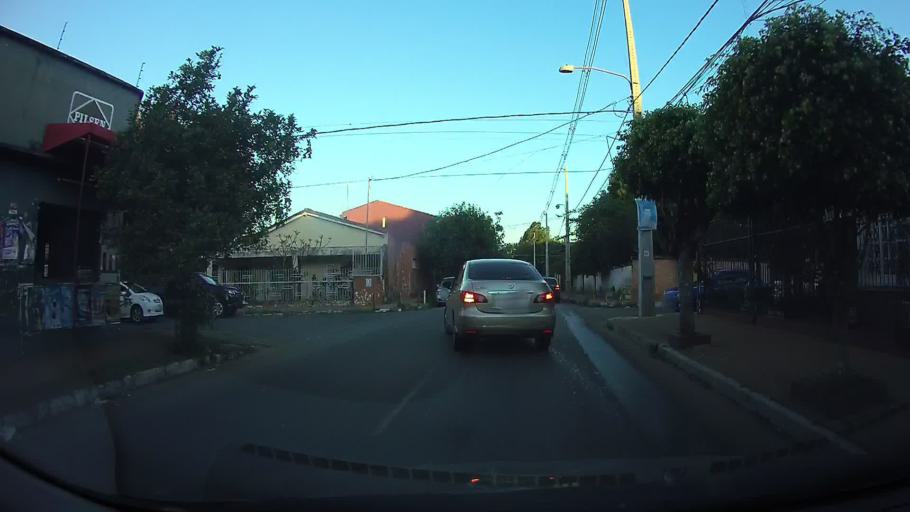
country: PY
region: Central
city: Fernando de la Mora
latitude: -25.3201
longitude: -57.5570
